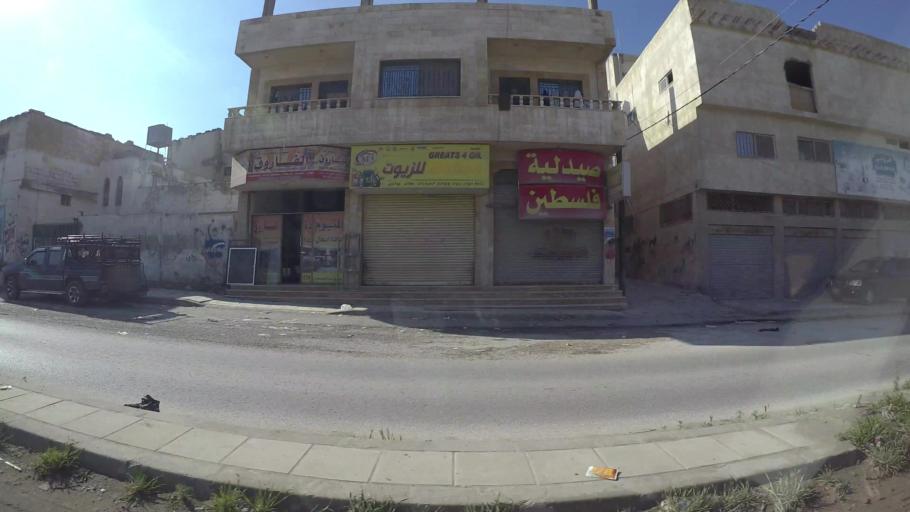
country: JO
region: Amman
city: Al Jubayhah
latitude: 32.0805
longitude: 35.8467
